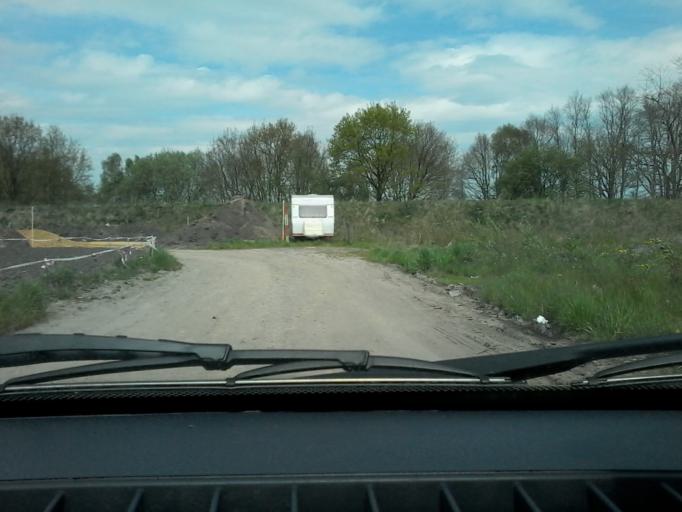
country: DE
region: Lower Saxony
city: Ahsen-Oetzen
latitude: 53.0066
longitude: 9.0840
